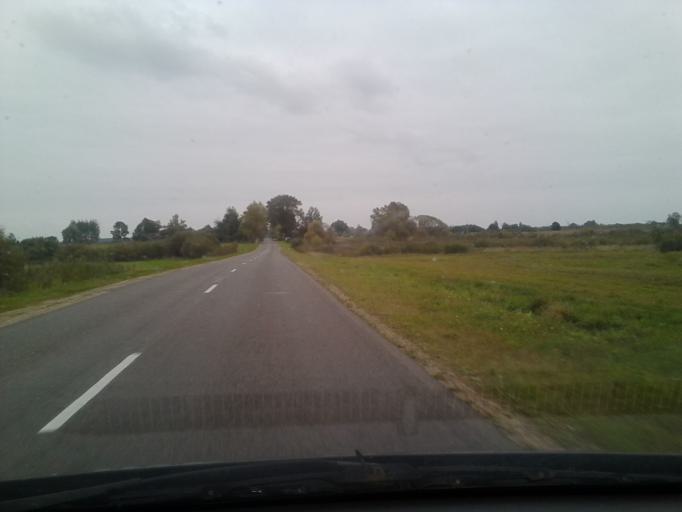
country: BY
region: Vitebsk
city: Pastavy
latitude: 55.1389
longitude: 26.9496
